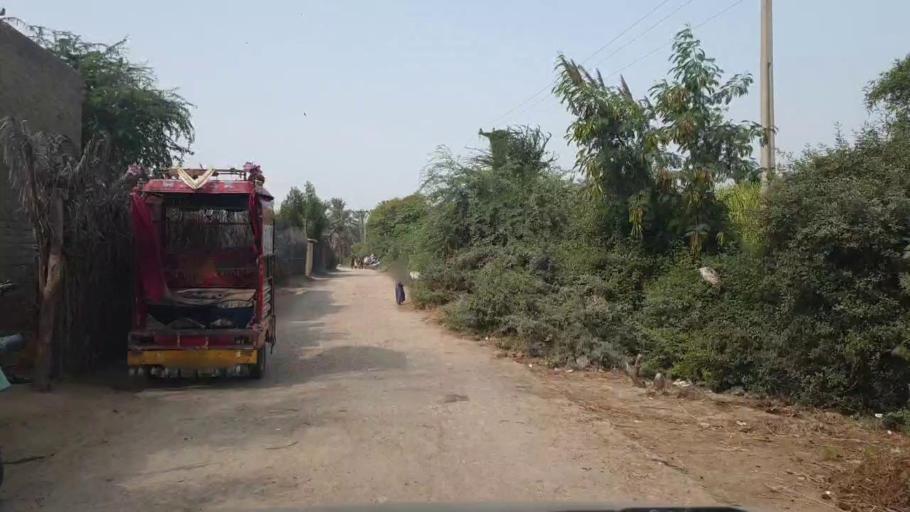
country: PK
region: Sindh
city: Tando Muhammad Khan
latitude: 25.1146
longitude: 68.3679
